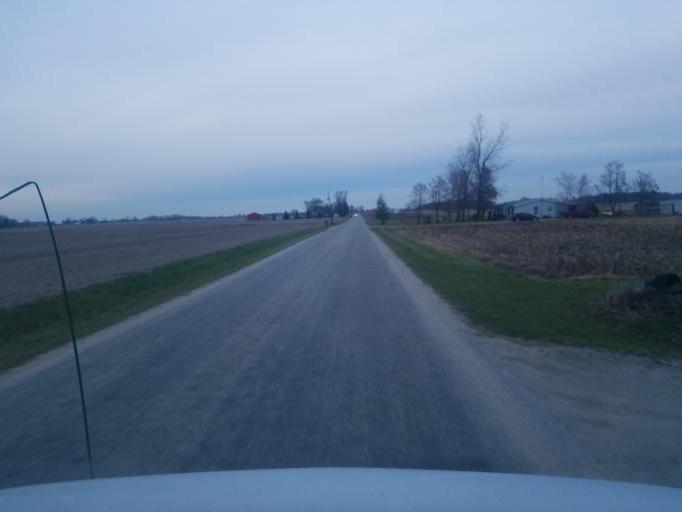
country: US
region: Indiana
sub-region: Adams County
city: Decatur
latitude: 40.7481
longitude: -84.8796
